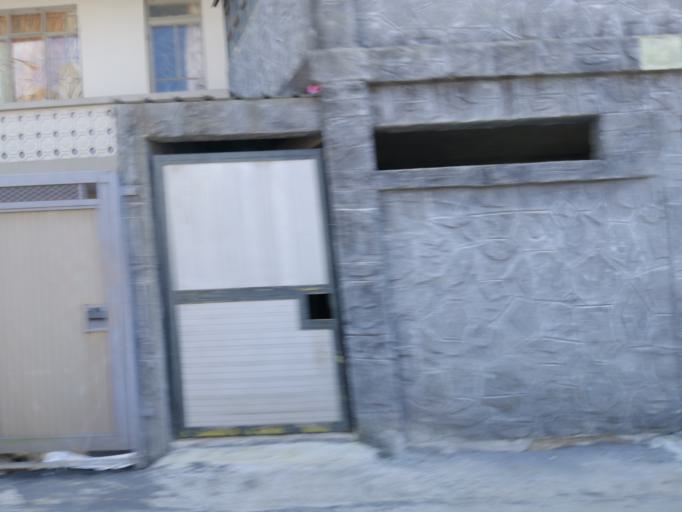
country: MU
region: Moka
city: Verdun
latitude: -20.2199
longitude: 57.5357
